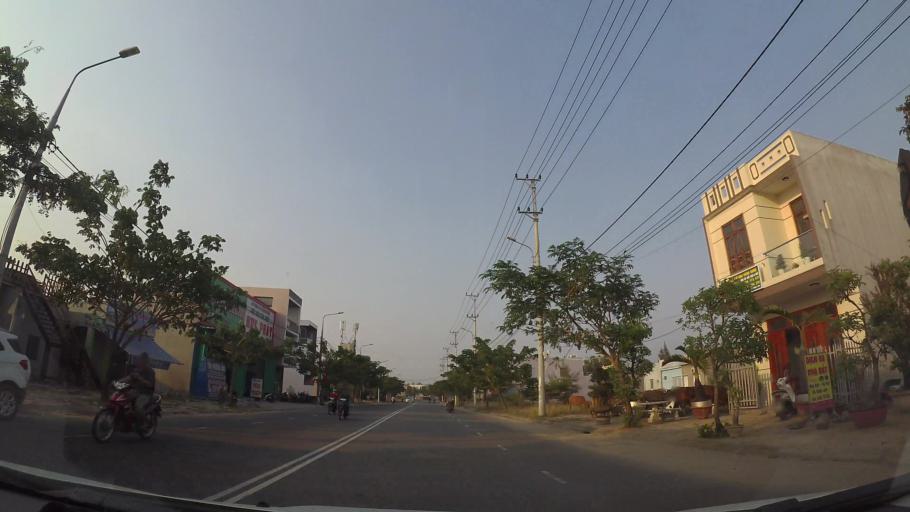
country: VN
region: Da Nang
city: Ngu Hanh Son
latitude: 15.9788
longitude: 108.2338
